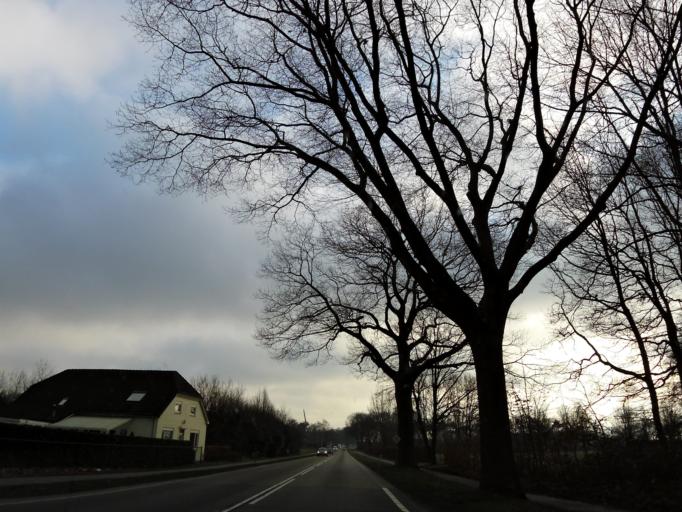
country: NL
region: North Brabant
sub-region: Gemeente Boxmeer
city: Boxmeer
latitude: 51.6572
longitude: 5.9896
